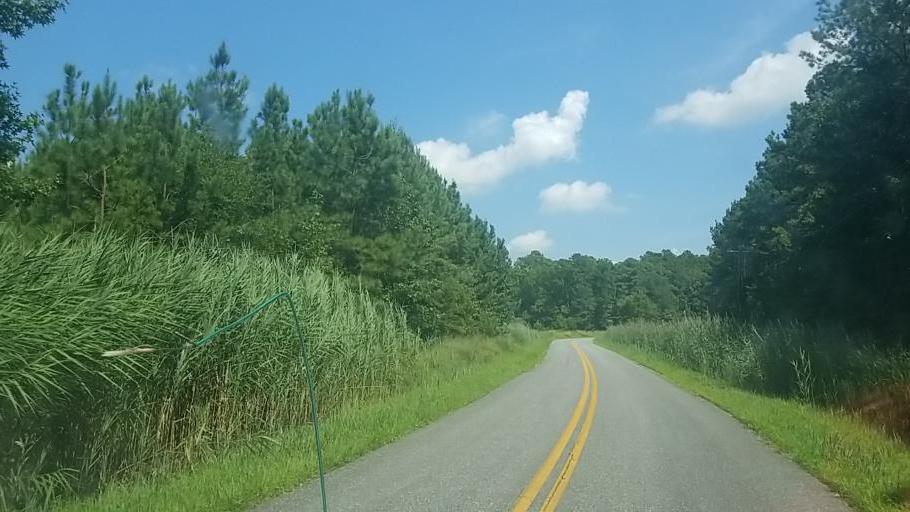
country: US
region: Maryland
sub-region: Dorchester County
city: Hurlock
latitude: 38.4335
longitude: -75.8921
